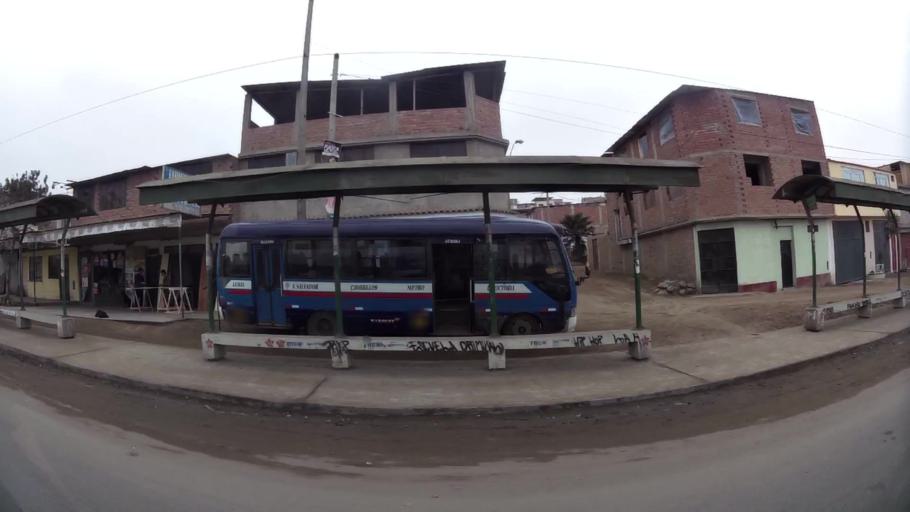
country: PE
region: Lima
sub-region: Lima
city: Surco
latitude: -12.2244
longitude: -76.9194
